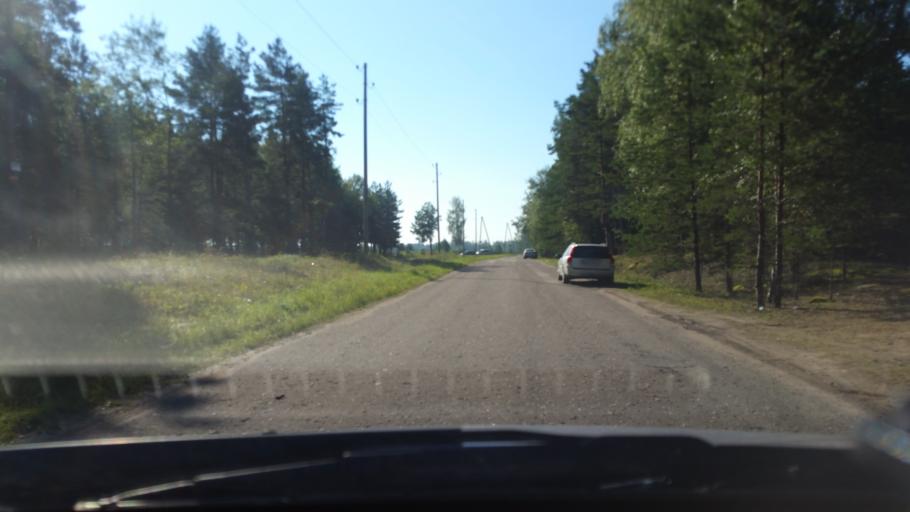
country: LV
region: Adazi
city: Adazi
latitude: 57.1194
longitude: 24.3619
